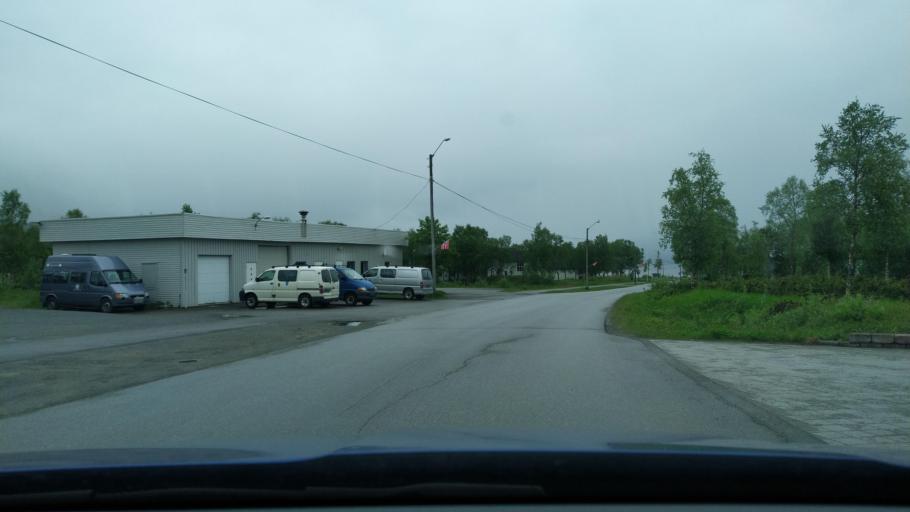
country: NO
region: Troms
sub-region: Dyroy
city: Brostadbotn
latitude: 69.0896
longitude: 17.7001
